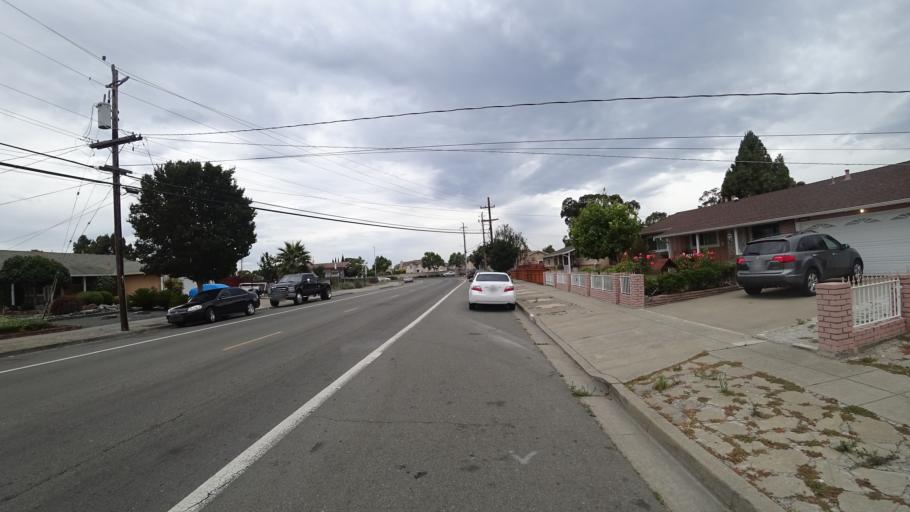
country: US
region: California
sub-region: Alameda County
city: Hayward
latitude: 37.6209
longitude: -122.0892
